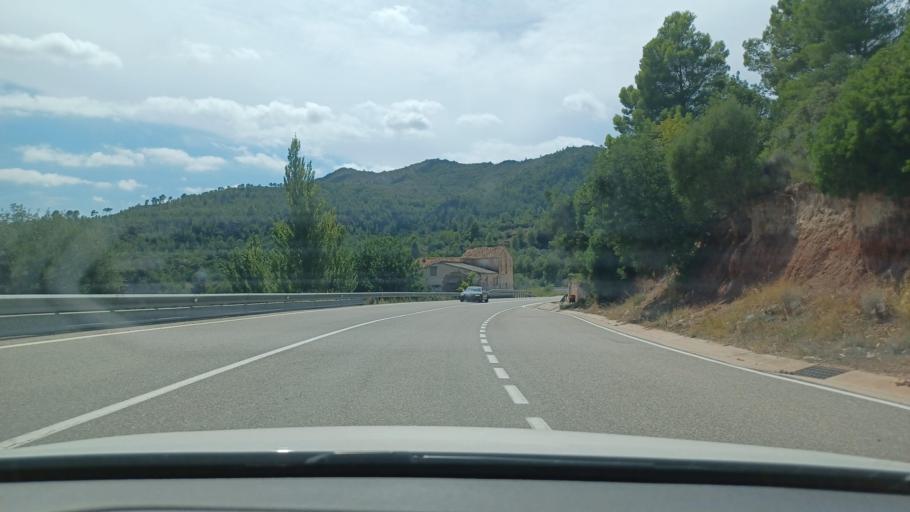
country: ES
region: Catalonia
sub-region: Provincia de Tarragona
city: Benifallet
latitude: 40.9459
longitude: 0.4612
